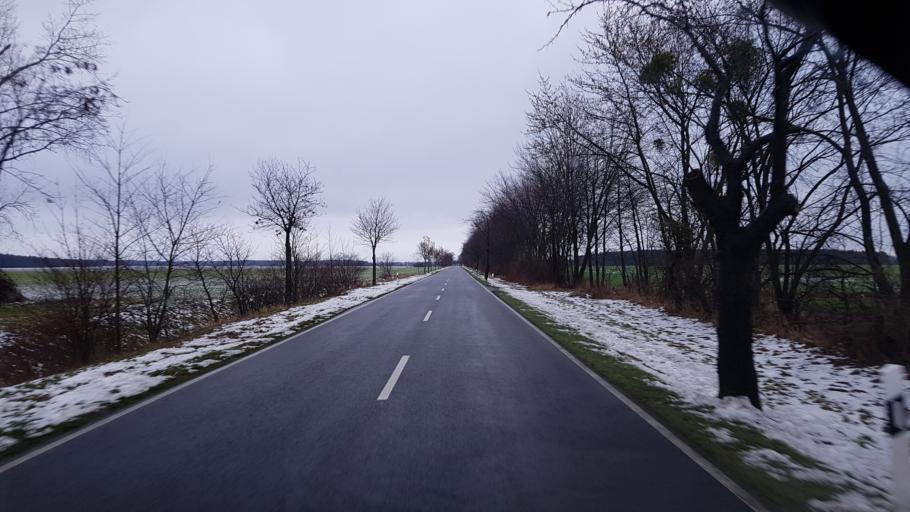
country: DE
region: Brandenburg
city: Luckau
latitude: 51.8501
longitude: 13.7712
